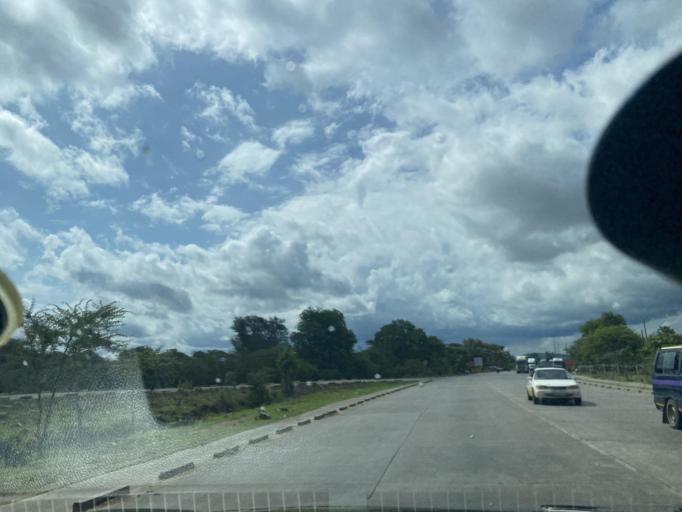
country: ZM
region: Lusaka
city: Kafue
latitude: -15.8448
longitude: 28.2422
